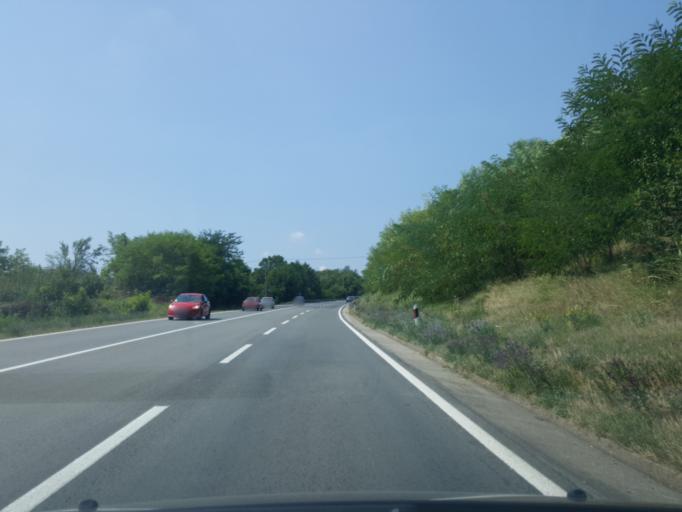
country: RS
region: Central Serbia
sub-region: Belgrade
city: Sopot
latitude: 44.5506
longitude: 20.6642
